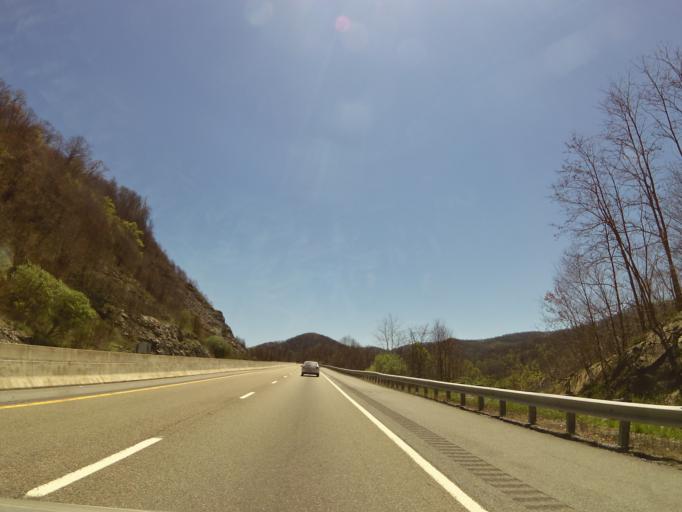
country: US
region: North Carolina
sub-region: Madison County
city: Mars Hill
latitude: 35.9687
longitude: -82.5528
